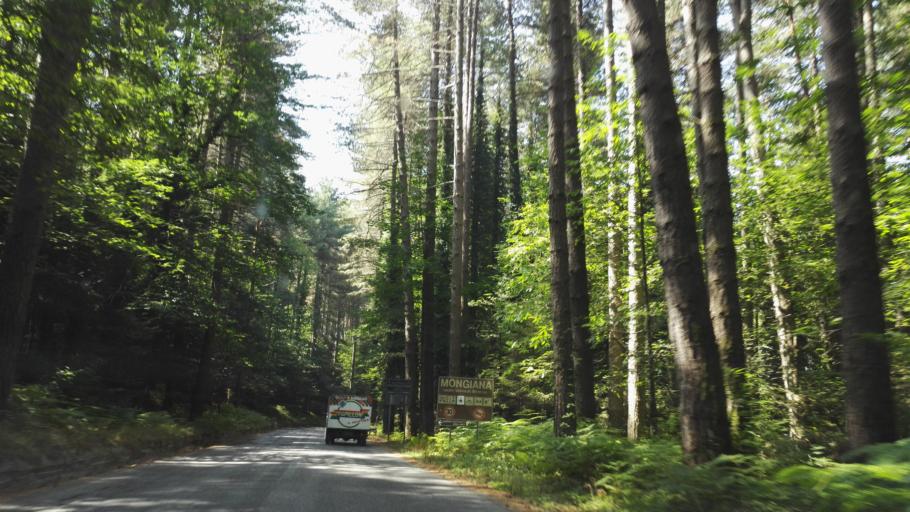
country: IT
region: Calabria
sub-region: Provincia di Vibo-Valentia
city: Mongiana
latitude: 38.5220
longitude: 16.3194
